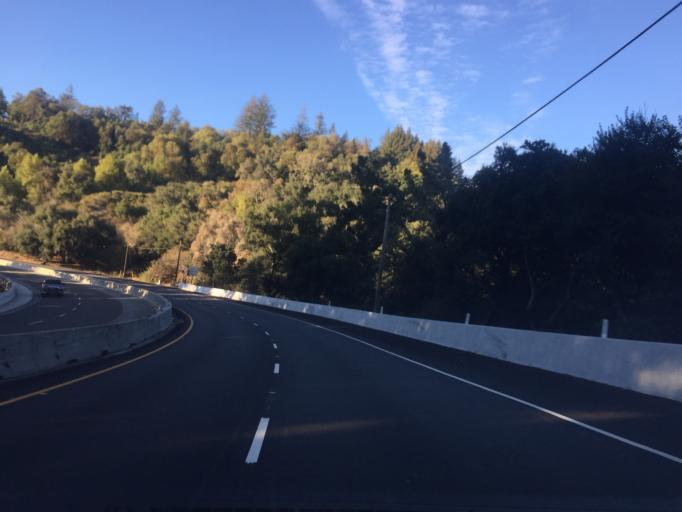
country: US
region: California
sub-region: Santa Clara County
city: Lexington Hills
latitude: 37.1045
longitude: -121.9749
